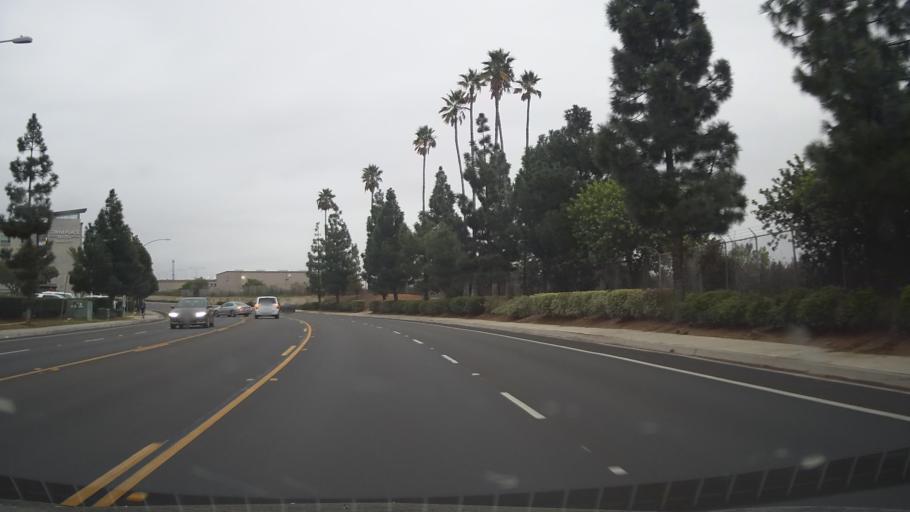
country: US
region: California
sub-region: San Diego County
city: San Diego
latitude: 32.8246
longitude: -117.1406
